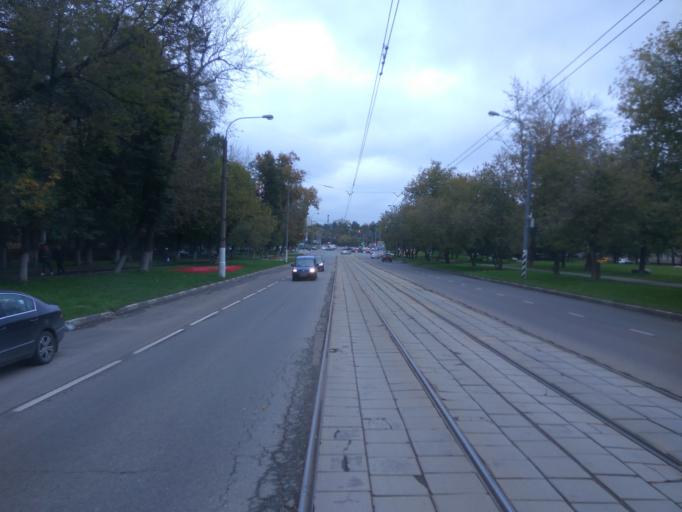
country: RU
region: Moscow
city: Kotlovka
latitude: 55.6614
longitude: 37.6110
